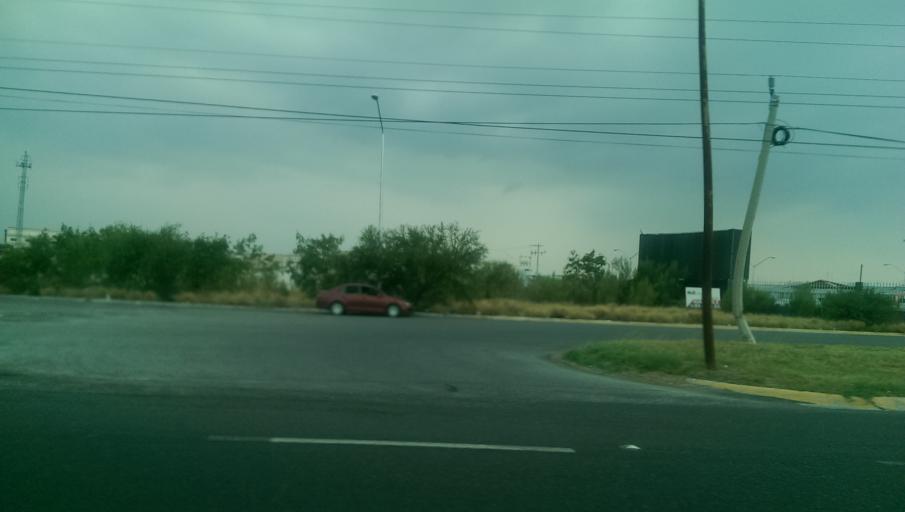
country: MX
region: Nuevo Leon
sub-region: Pesqueria
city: Ladrillera (Entronque Pesqueria)
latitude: 25.7841
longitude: -100.1310
